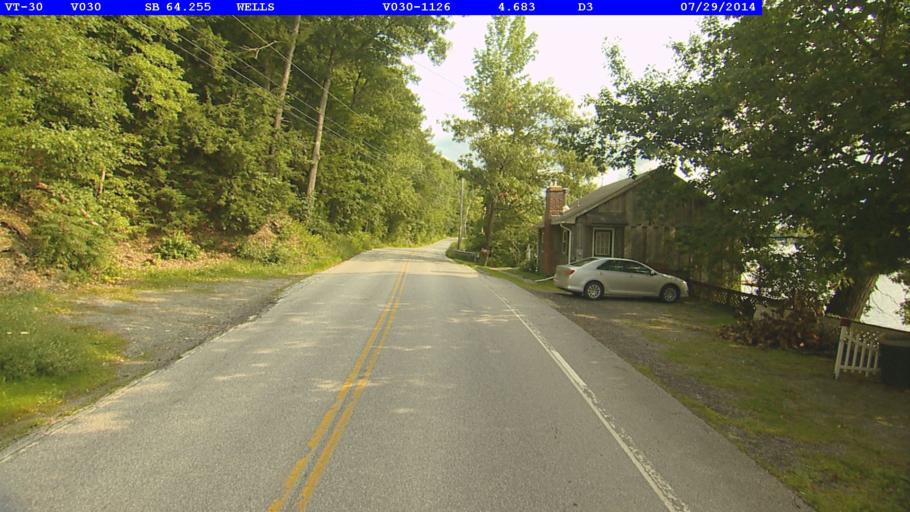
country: US
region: Vermont
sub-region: Rutland County
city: Poultney
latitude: 43.4582
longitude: -73.2056
